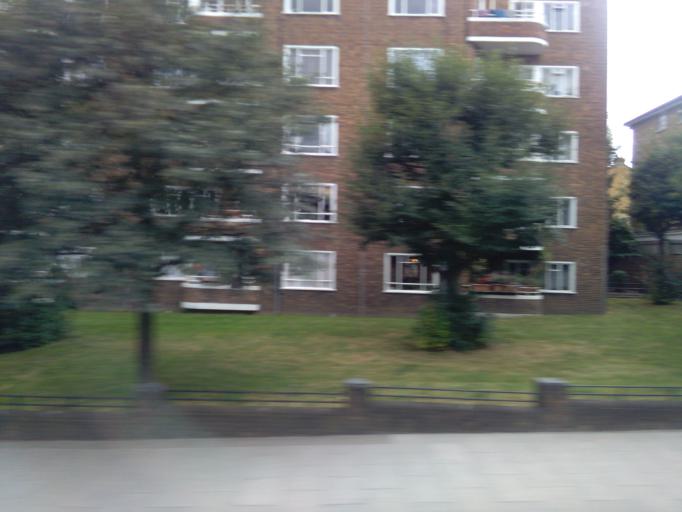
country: GB
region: England
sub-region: Greater London
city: Brixton Hill
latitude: 51.4499
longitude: -0.1481
